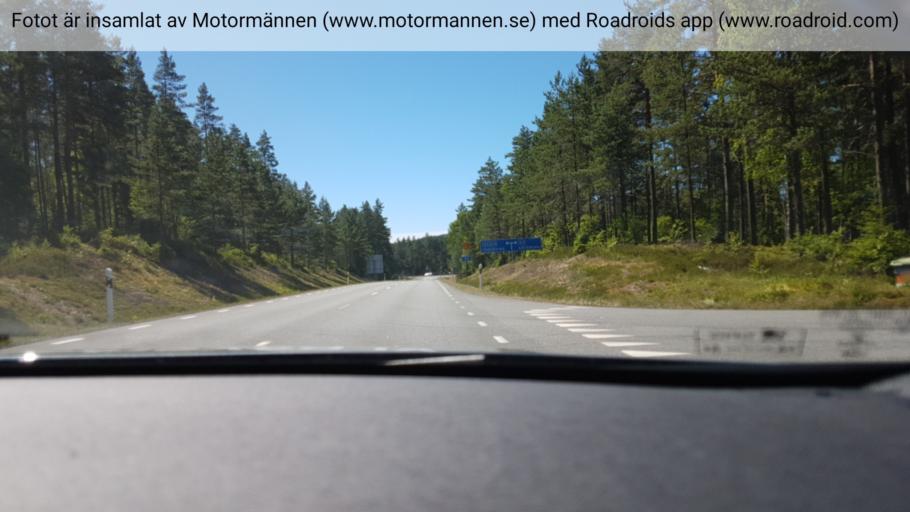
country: SE
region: Joenkoeping
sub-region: Mullsjo Kommun
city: Mullsjoe
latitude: 57.7666
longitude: 13.8312
